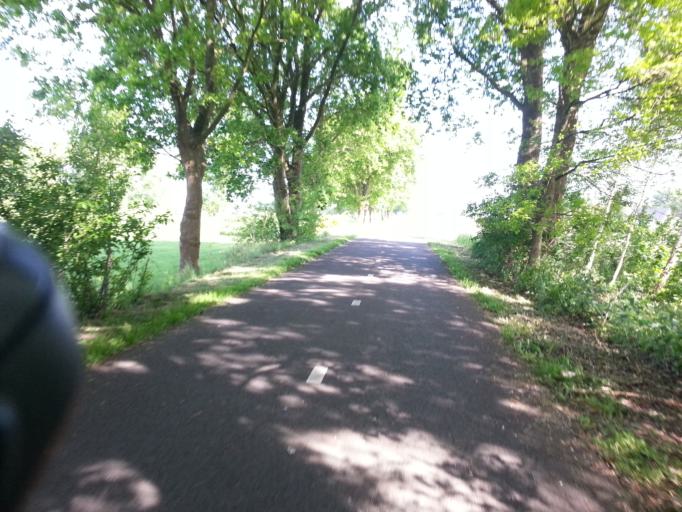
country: NL
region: Gelderland
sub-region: Berkelland
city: Eibergen
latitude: 52.1107
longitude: 6.6375
